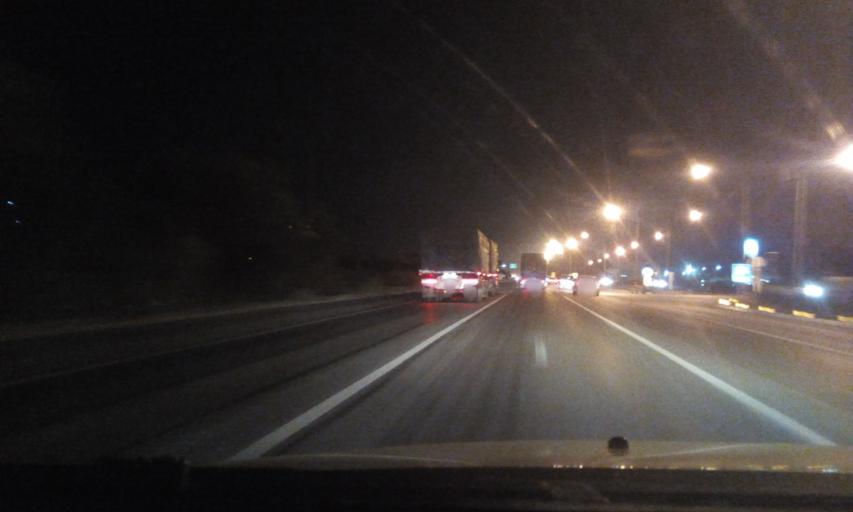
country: TH
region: Ang Thong
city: Chaiyo
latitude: 14.7285
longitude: 100.4551
